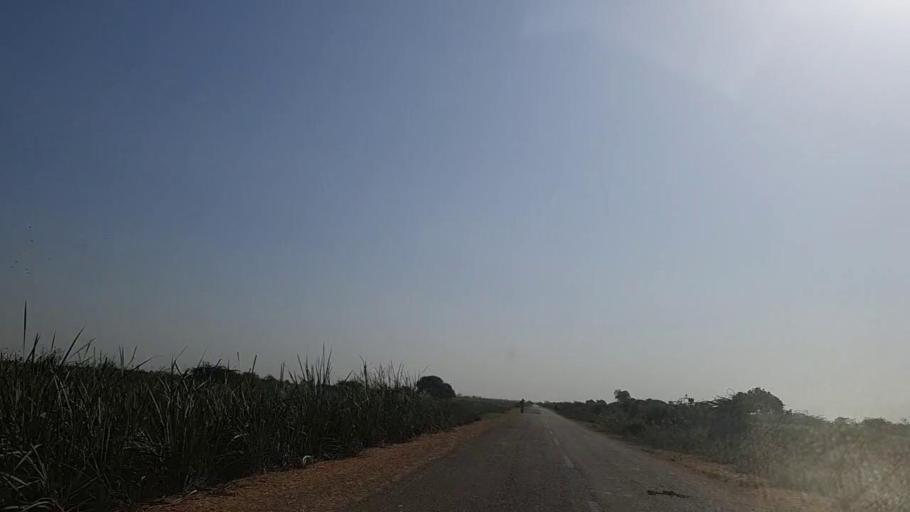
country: PK
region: Sindh
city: Jati
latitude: 24.4531
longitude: 68.2641
